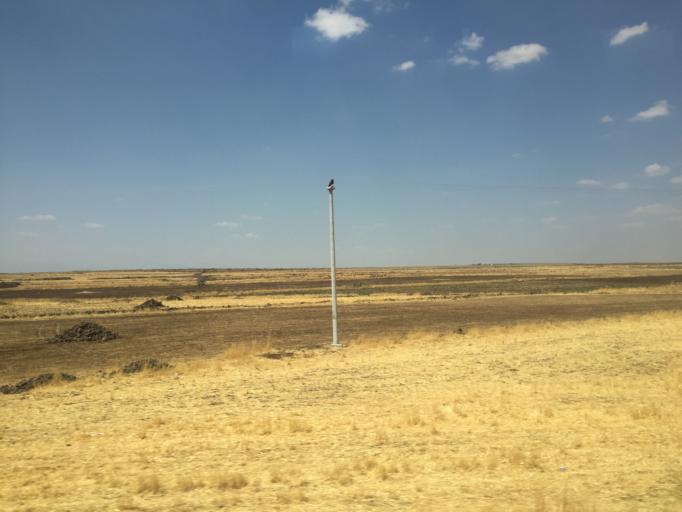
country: TR
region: Sanliurfa
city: Siverek
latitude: 37.7698
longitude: 39.4367
